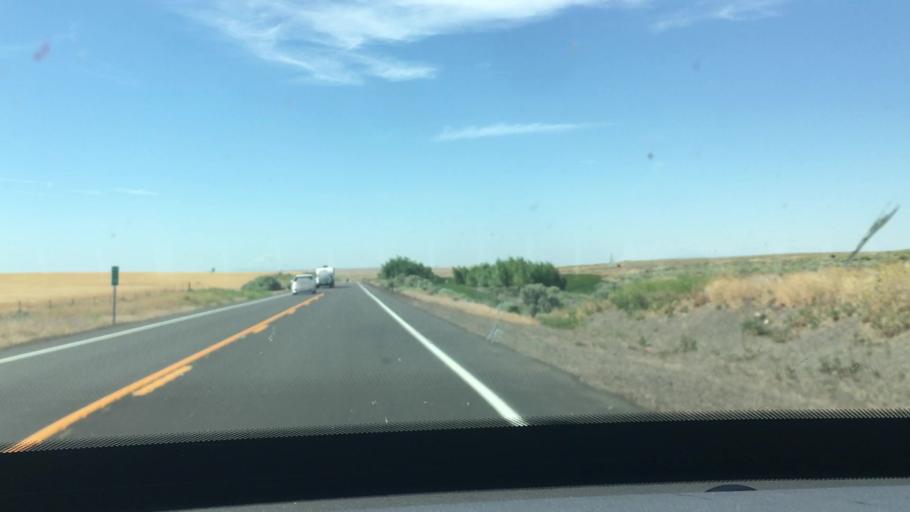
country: US
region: Oregon
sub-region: Sherman County
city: Moro
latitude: 45.3334
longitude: -120.7701
